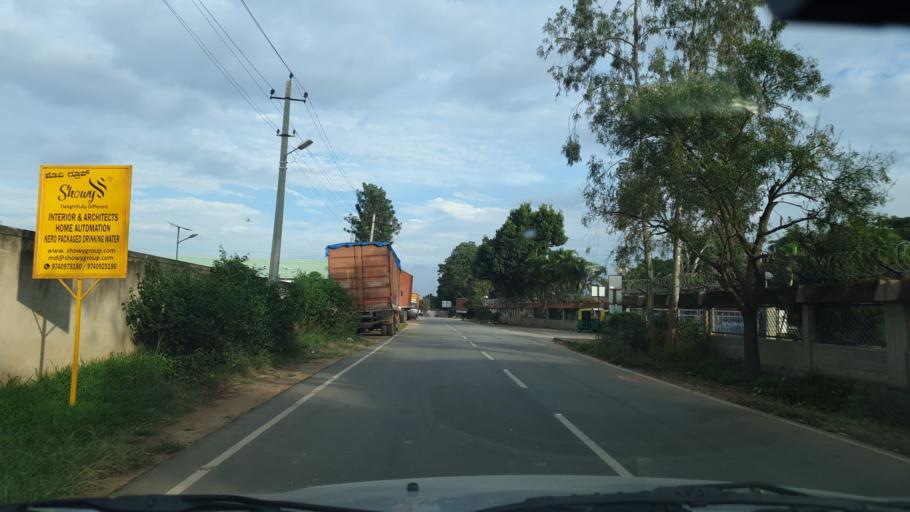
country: IN
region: Karnataka
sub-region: Bangalore Rural
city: Devanhalli
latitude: 13.1889
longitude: 77.6421
